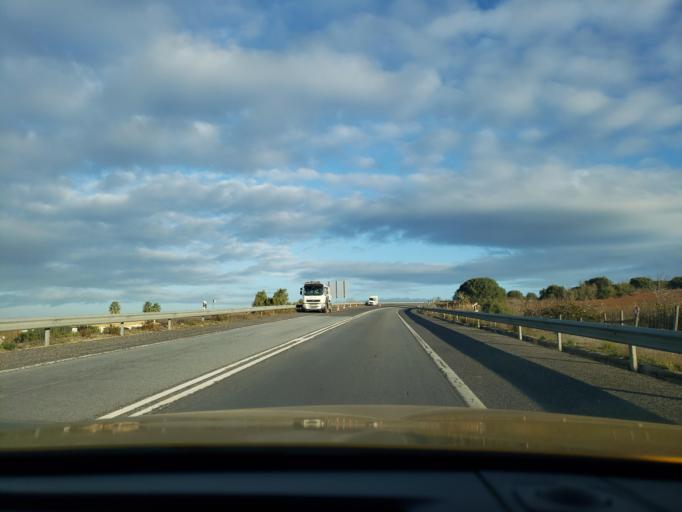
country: PT
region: Faro
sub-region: Portimao
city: Alvor
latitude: 37.1646
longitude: -8.5698
